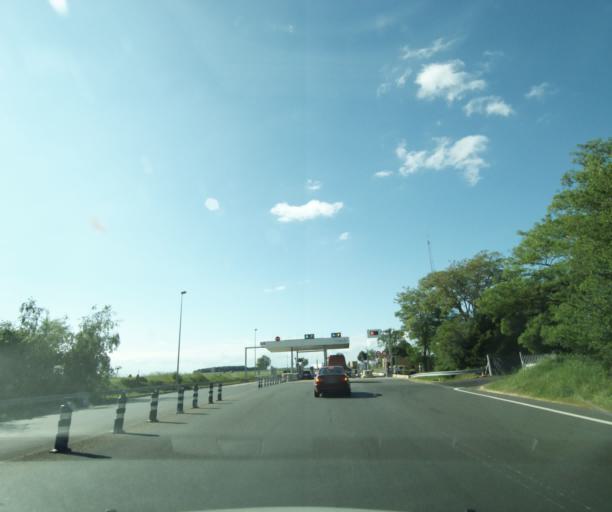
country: FR
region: Centre
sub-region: Departement d'Eure-et-Loir
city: Janville
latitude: 48.2048
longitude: 1.8465
